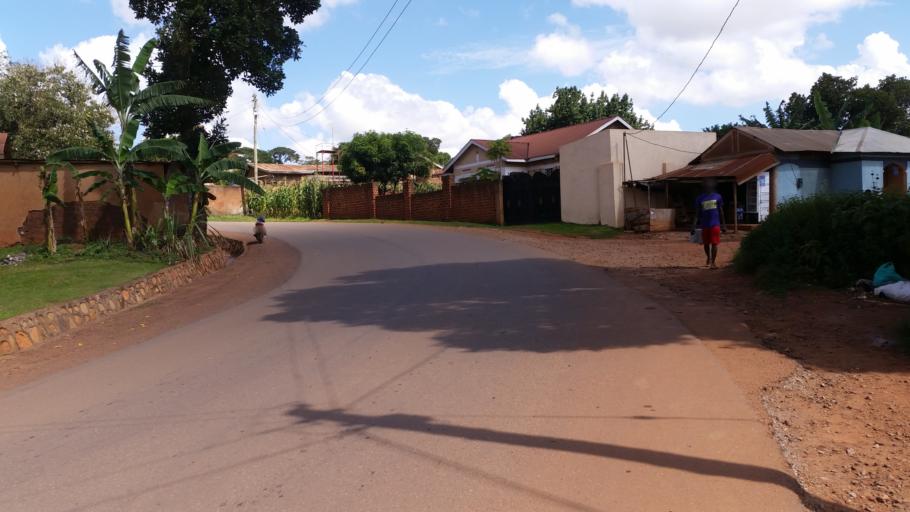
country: UG
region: Central Region
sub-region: Wakiso District
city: Kireka
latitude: 0.3568
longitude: 32.6368
